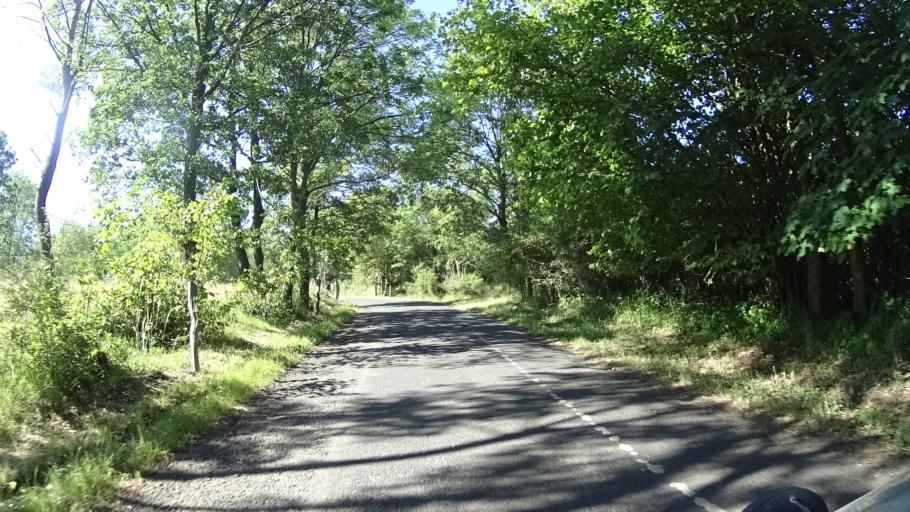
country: CZ
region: Ustecky
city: Zitenice
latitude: 50.5860
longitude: 14.1246
